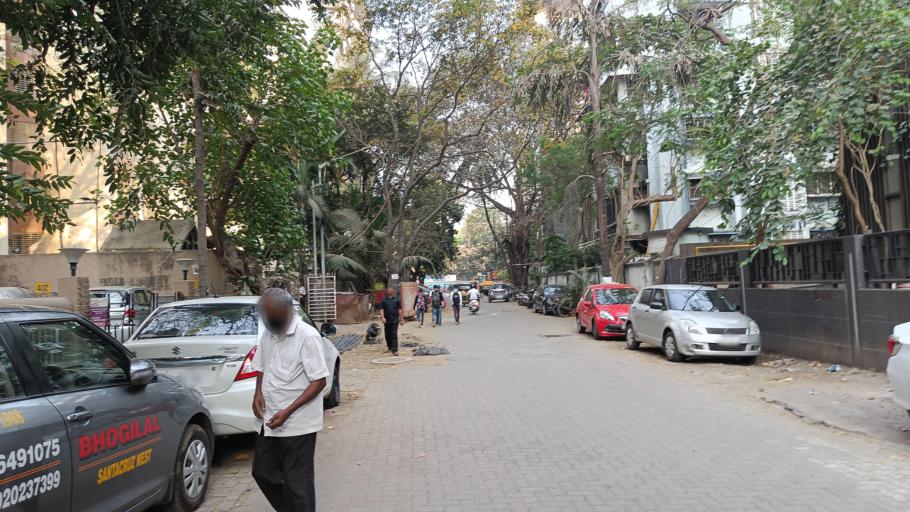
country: IN
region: Maharashtra
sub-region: Mumbai Suburban
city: Mumbai
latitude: 19.0819
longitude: 72.8369
